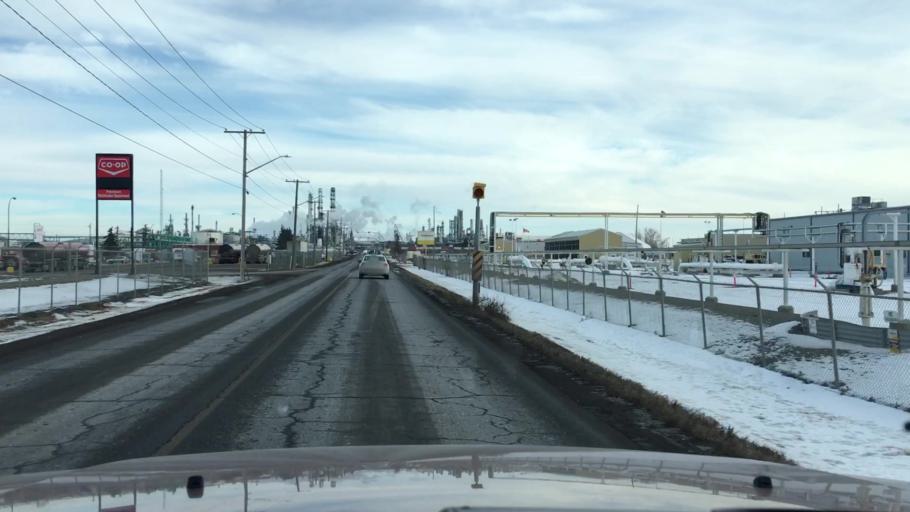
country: CA
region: Saskatchewan
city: Regina
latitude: 50.4843
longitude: -104.5882
